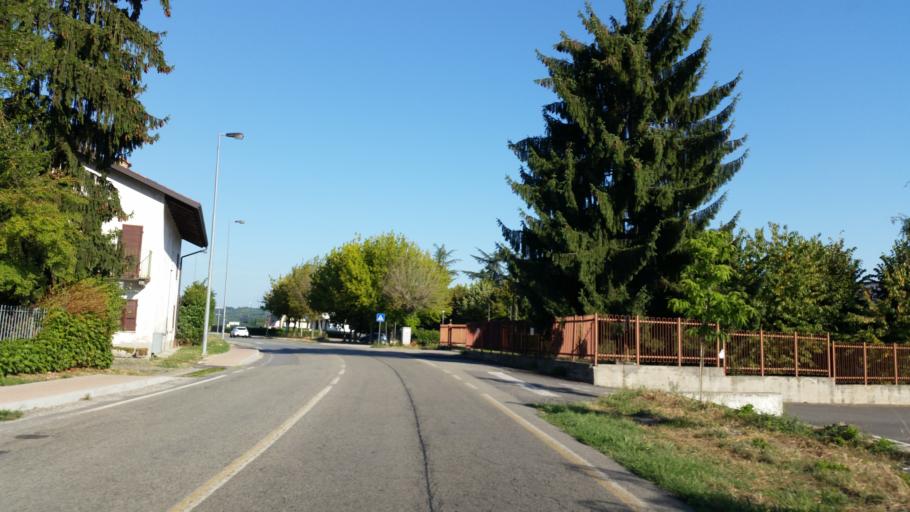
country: IT
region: Piedmont
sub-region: Provincia di Cuneo
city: Roddi
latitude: 44.6812
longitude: 7.9840
